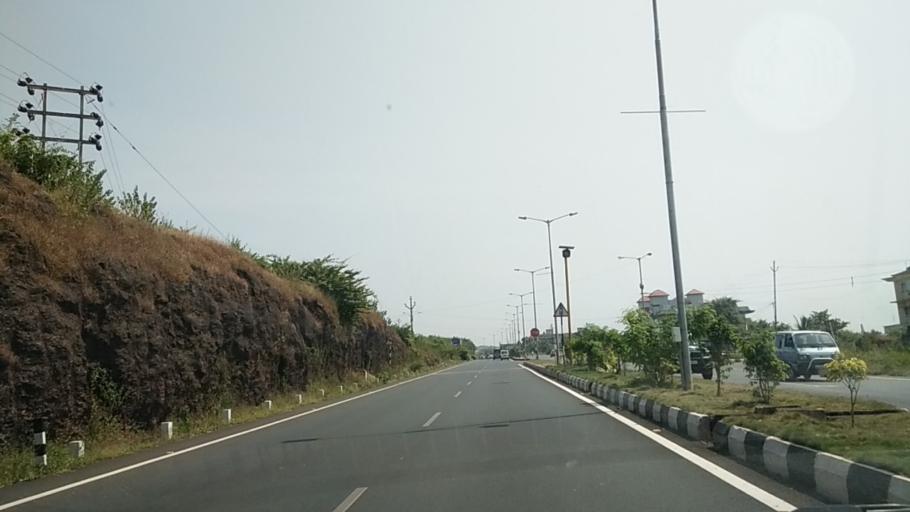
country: IN
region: Goa
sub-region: South Goa
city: Sancoale
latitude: 15.3727
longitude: 73.8915
